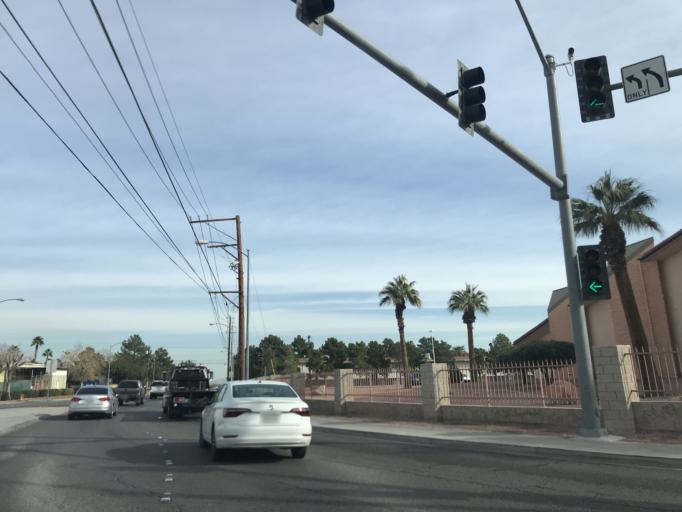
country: US
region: Nevada
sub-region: Clark County
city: Paradise
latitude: 36.0972
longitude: -115.1702
